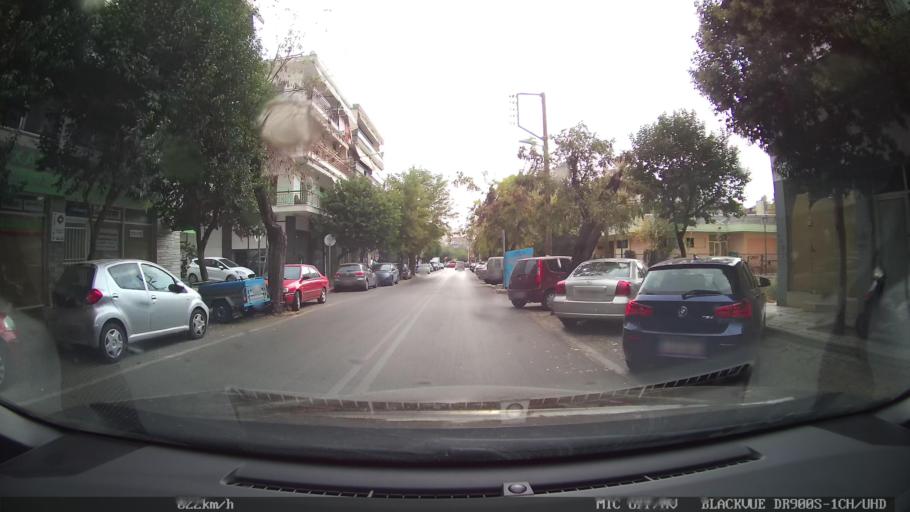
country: GR
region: Central Macedonia
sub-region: Nomos Thessalonikis
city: Triandria
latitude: 40.6088
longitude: 22.9752
